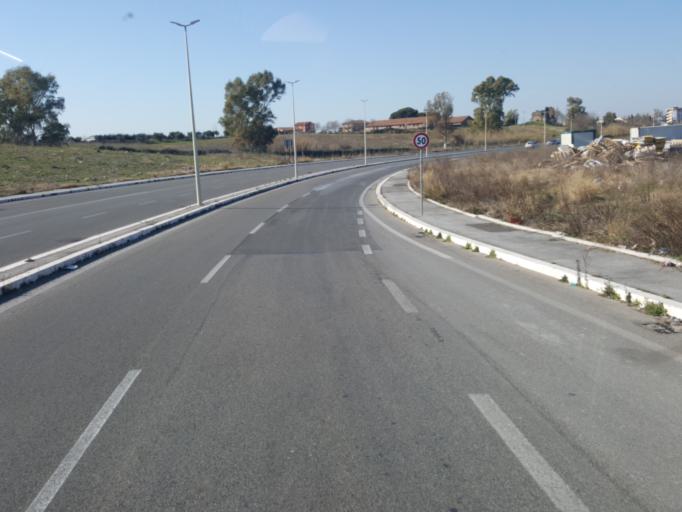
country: IT
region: Latium
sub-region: Citta metropolitana di Roma Capitale
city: Setteville
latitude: 41.8838
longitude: 12.6057
